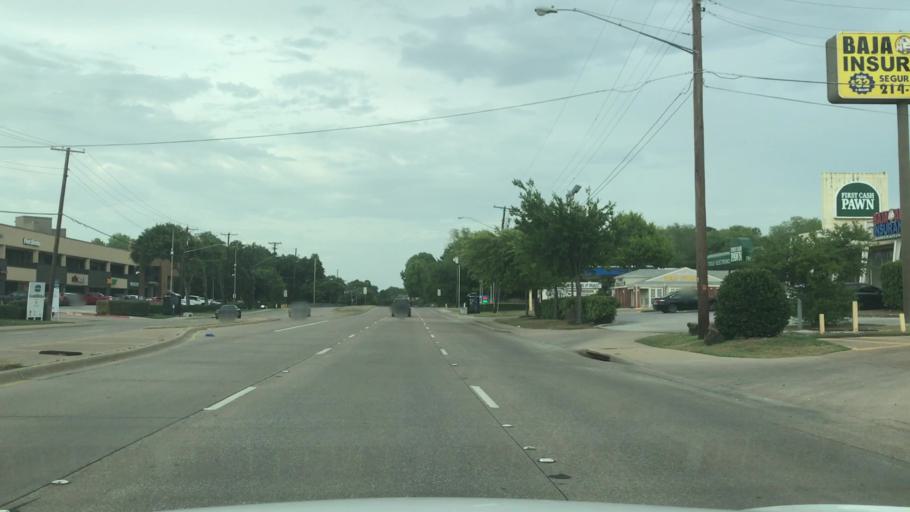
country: US
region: Texas
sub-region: Dallas County
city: Highland Park
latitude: 32.8660
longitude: -96.7421
